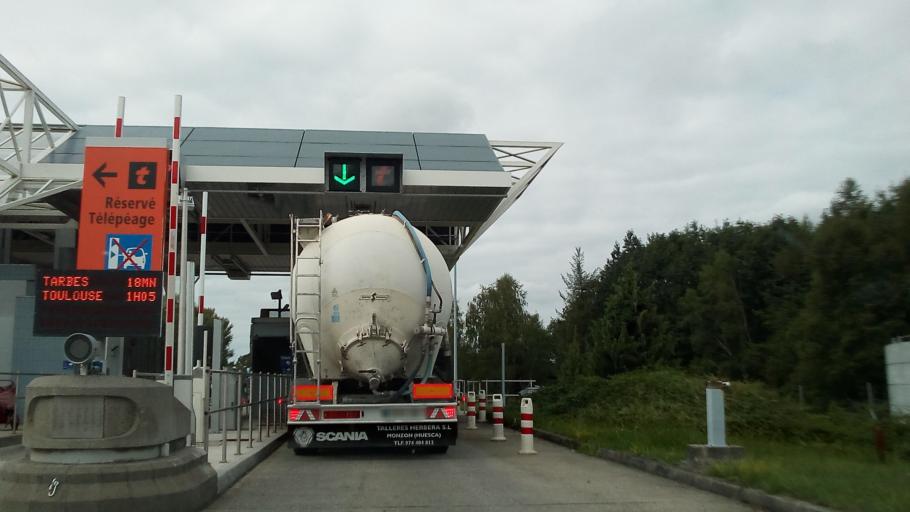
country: FR
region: Midi-Pyrenees
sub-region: Departement des Hautes-Pyrenees
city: La Barthe-de-Neste
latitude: 43.0976
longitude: 0.3904
